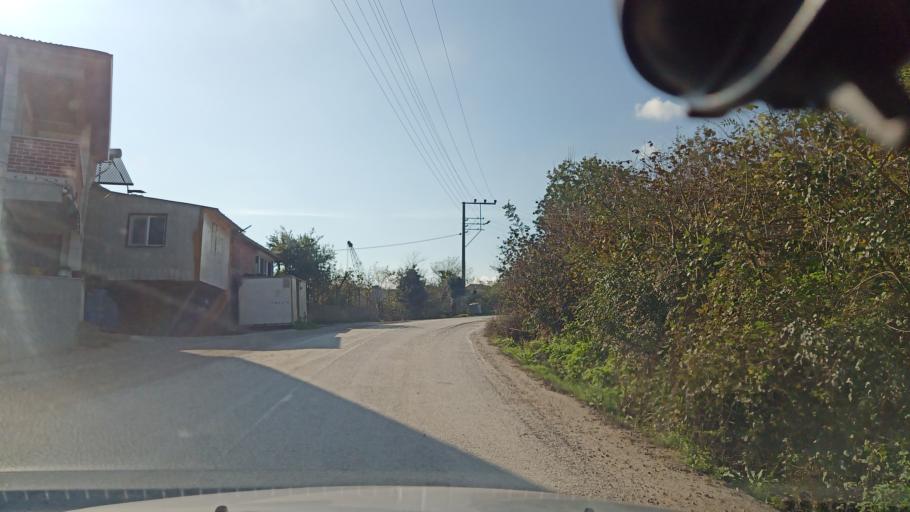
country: TR
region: Sakarya
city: Ferizli
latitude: 41.0928
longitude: 30.4561
